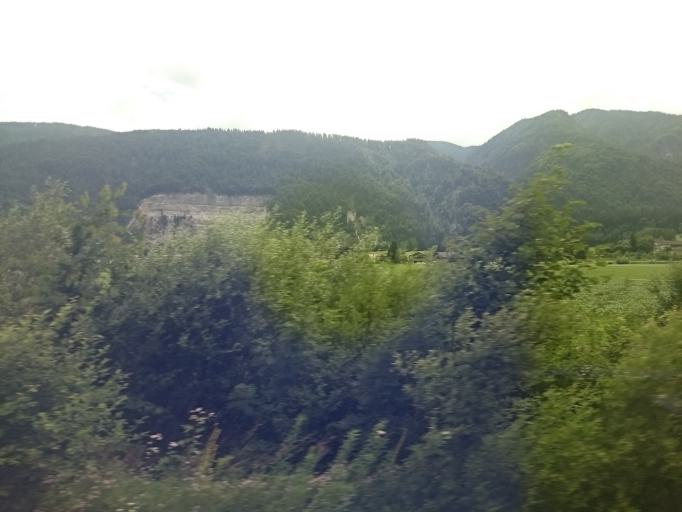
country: AT
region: Tyrol
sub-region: Politischer Bezirk Kufstein
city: Worgl
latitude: 47.4830
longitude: 12.0387
